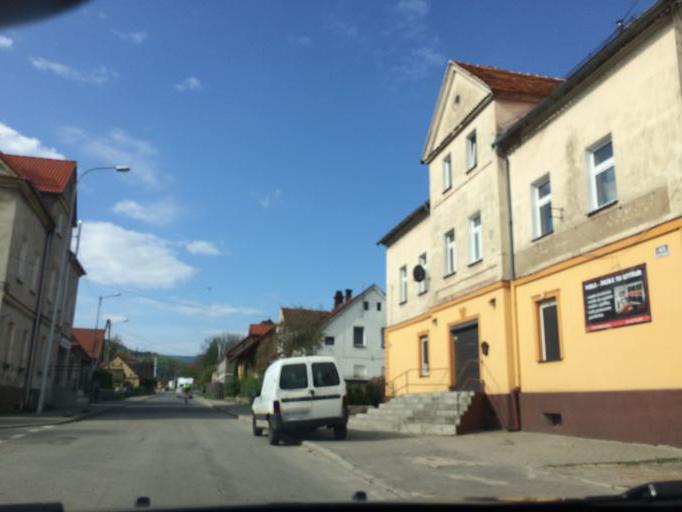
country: PL
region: Lower Silesian Voivodeship
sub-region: Powiat dzierzoniowski
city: Pieszyce
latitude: 50.7075
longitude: 16.5752
